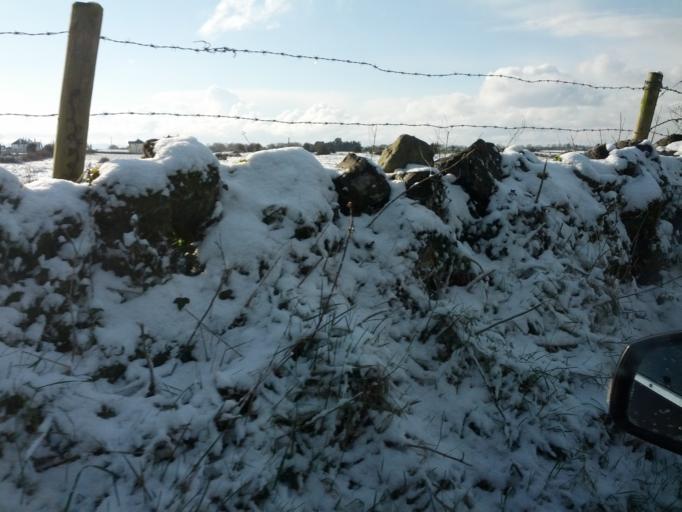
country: IE
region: Connaught
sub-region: County Galway
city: Athenry
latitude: 53.2002
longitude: -8.8074
